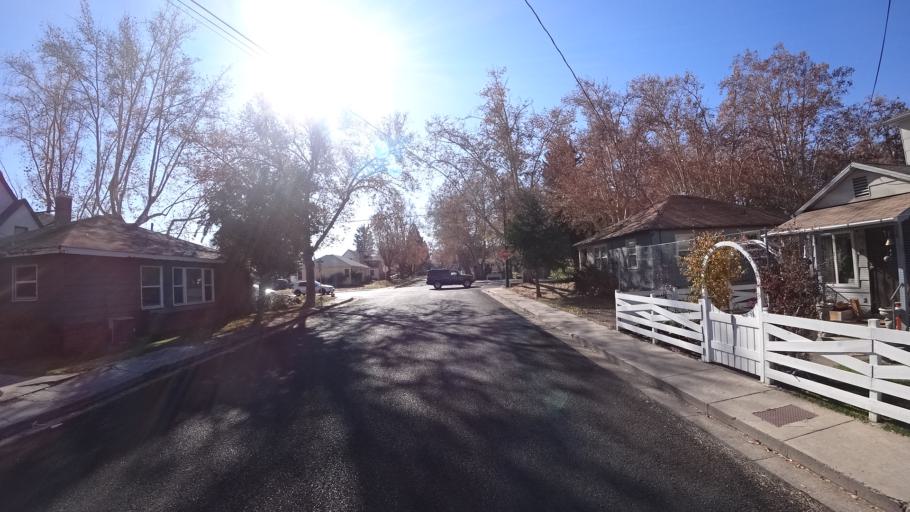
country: US
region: California
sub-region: Siskiyou County
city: Yreka
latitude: 41.7330
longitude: -122.6404
